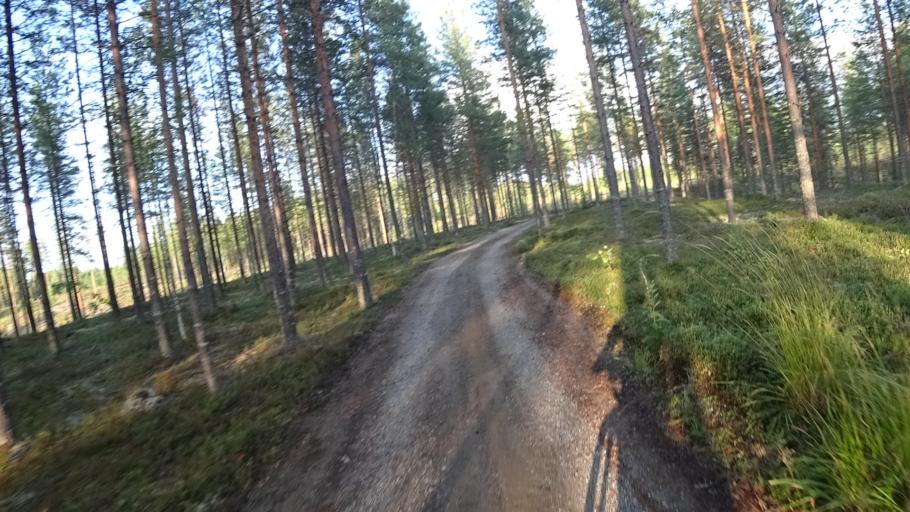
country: FI
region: North Karelia
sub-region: Joensuu
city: Ilomantsi
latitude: 62.6335
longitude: 31.0783
